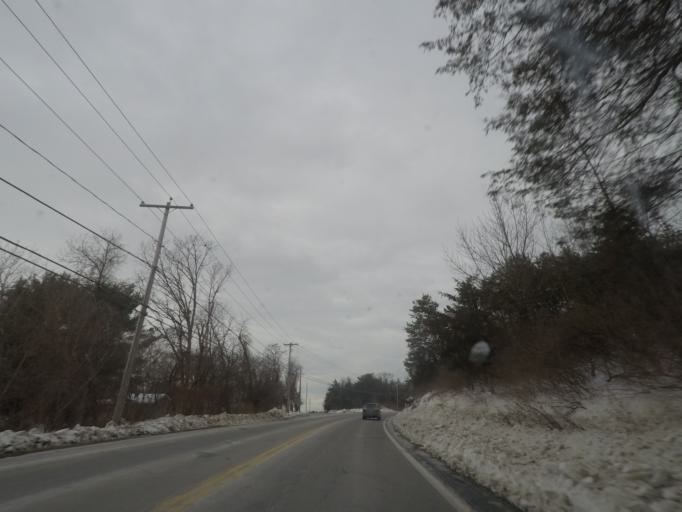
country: US
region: New York
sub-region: Columbia County
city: Kinderhook
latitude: 42.3712
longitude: -73.7329
